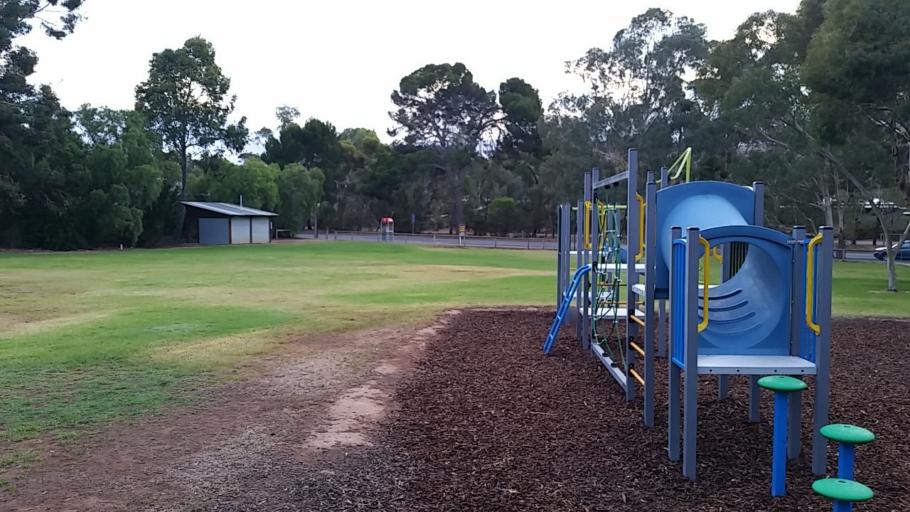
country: AU
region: South Australia
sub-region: Mount Barker
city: Callington
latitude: -35.0712
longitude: 139.0133
